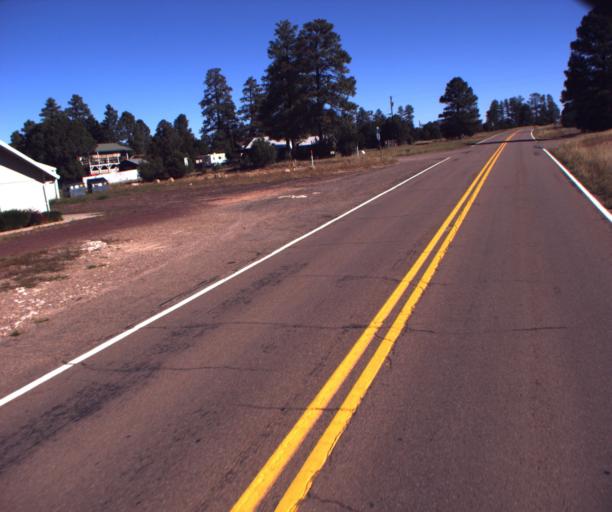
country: US
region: Arizona
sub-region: Navajo County
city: Heber-Overgaard
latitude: 34.4211
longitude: -110.5688
